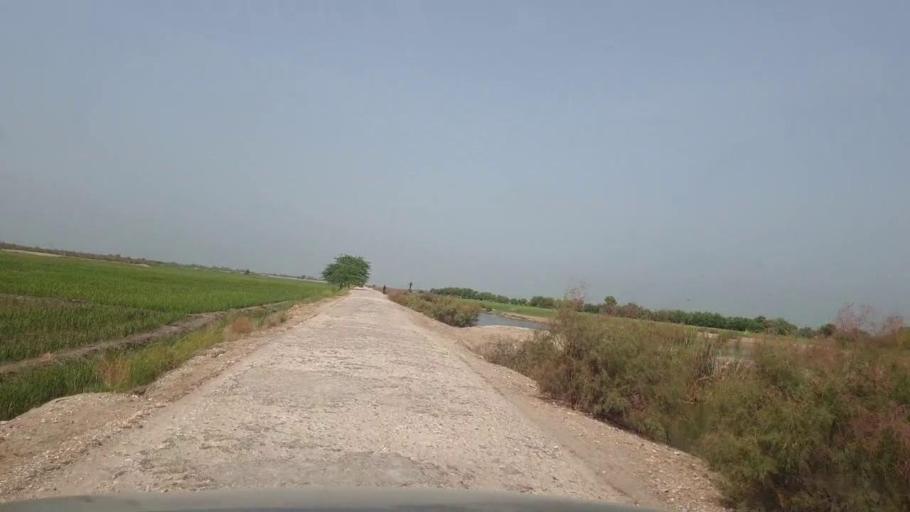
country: PK
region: Sindh
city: Garhi Yasin
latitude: 27.9168
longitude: 68.4278
